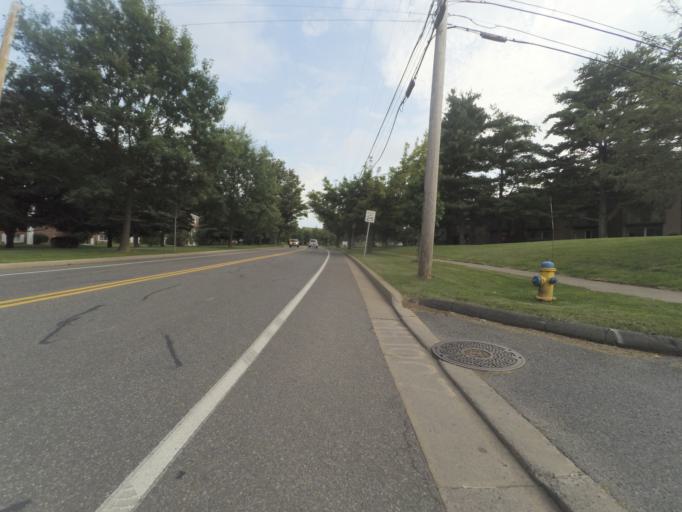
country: US
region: Pennsylvania
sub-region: Centre County
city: State College
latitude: 40.7788
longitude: -77.8546
